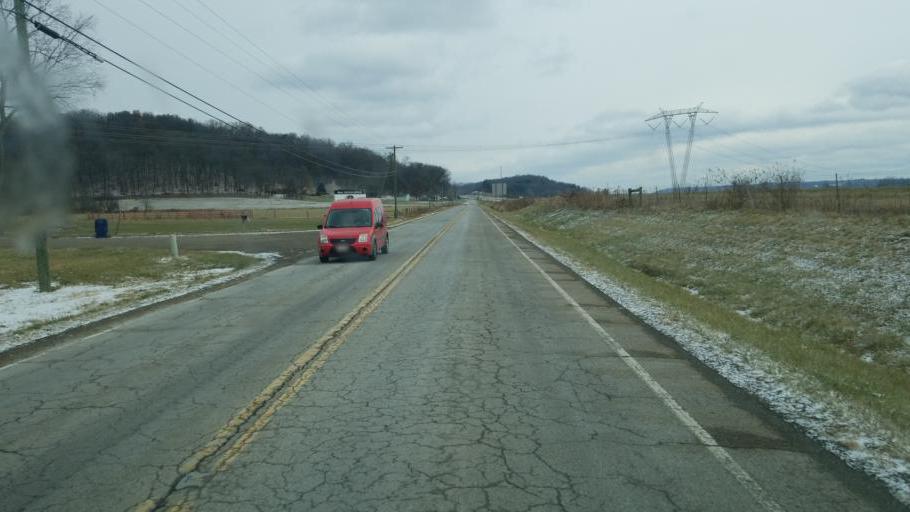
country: US
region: Ohio
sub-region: Muskingum County
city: Frazeysburg
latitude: 40.1104
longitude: -82.1679
